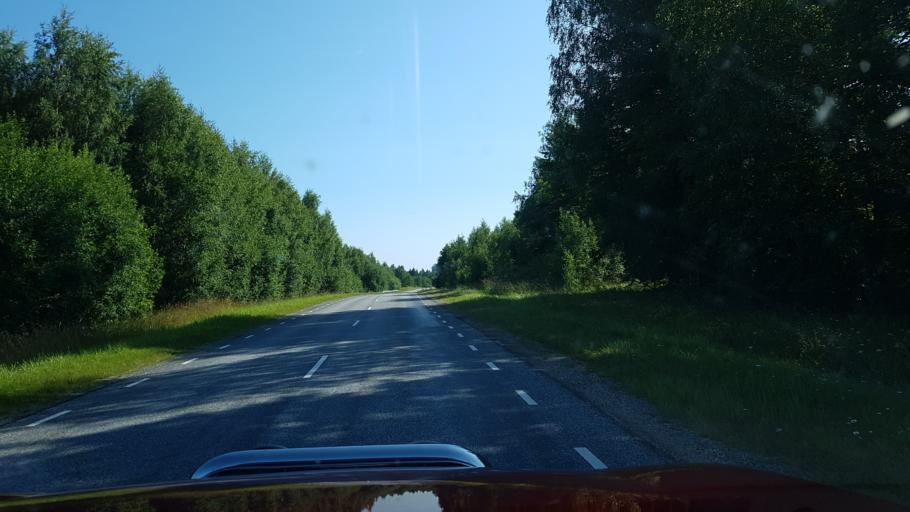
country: EE
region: Vorumaa
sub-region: Voru linn
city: Voru
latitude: 57.9770
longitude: 26.8521
